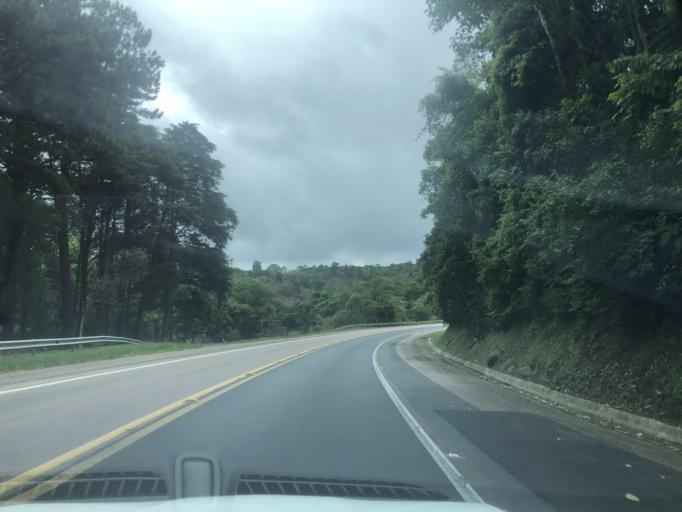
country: BR
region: Parana
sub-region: Araucaria
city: Araucaria
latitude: -25.8661
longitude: -49.4123
